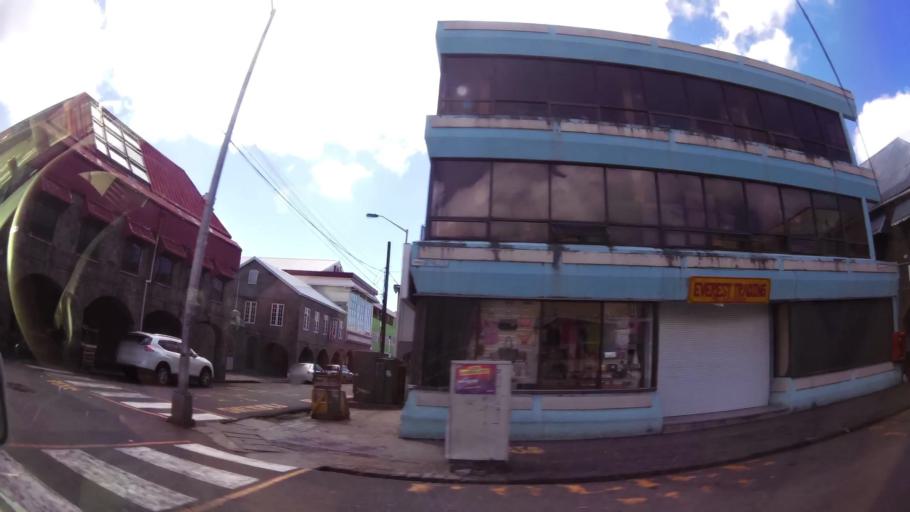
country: VC
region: Saint George
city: Kingstown
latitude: 13.1563
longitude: -61.2271
